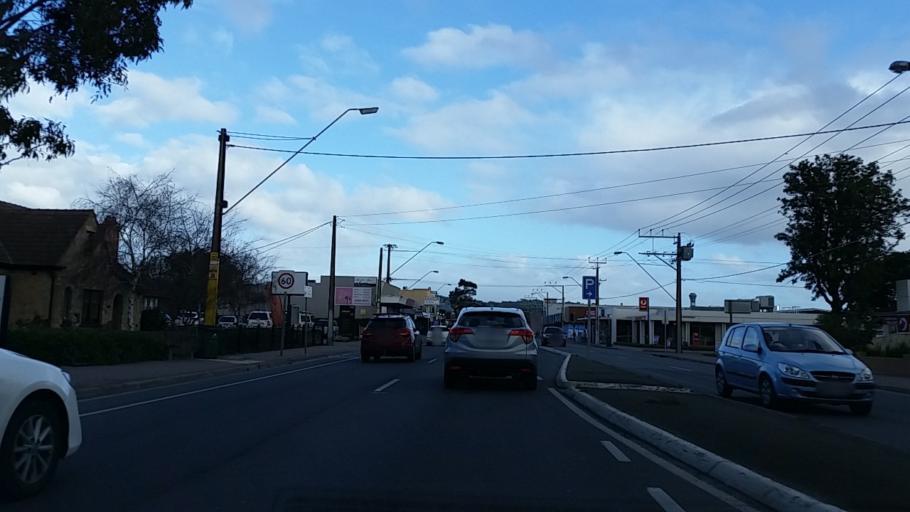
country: AU
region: South Australia
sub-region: Adelaide
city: Brighton
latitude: -35.0202
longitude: 138.5232
